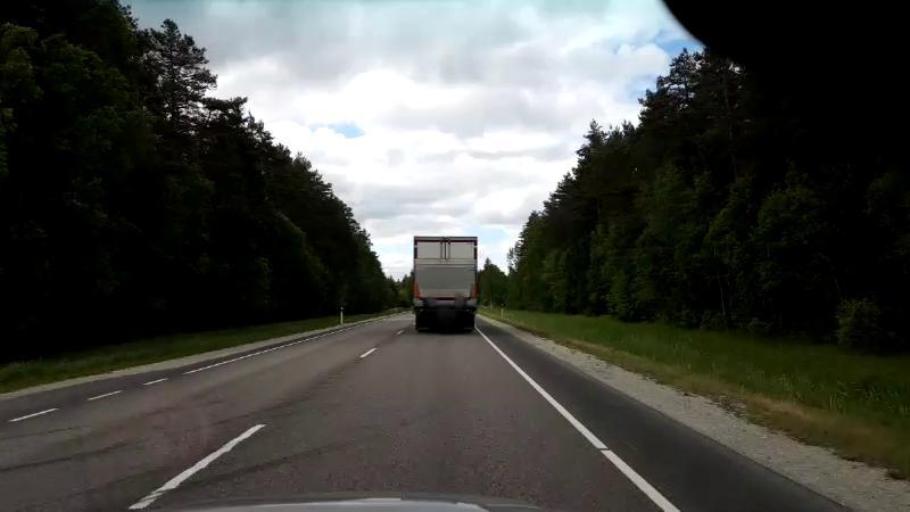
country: EE
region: Raplamaa
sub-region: Maerjamaa vald
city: Marjamaa
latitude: 58.7525
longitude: 24.4233
